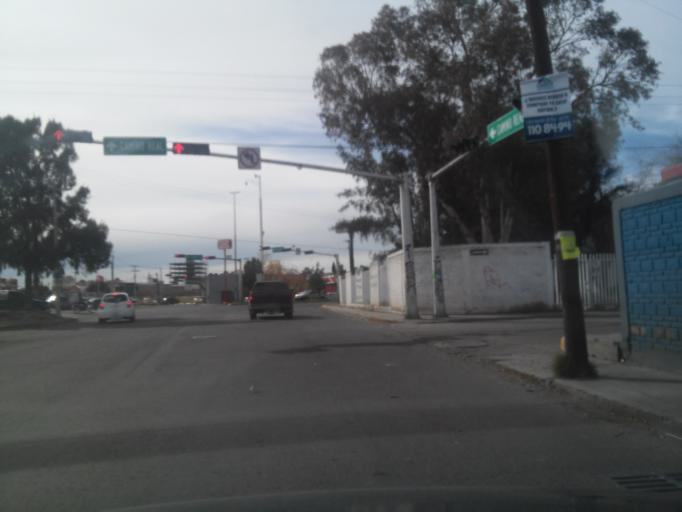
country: MX
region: Durango
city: Victoria de Durango
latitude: 24.0074
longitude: -104.6580
